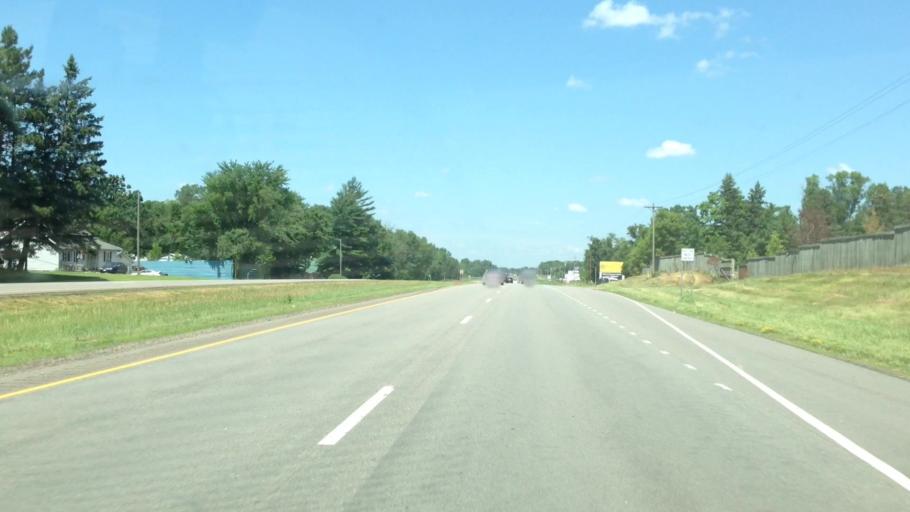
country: US
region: Minnesota
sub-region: Sherburne County
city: Zimmerman
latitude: 45.4236
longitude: -93.5688
